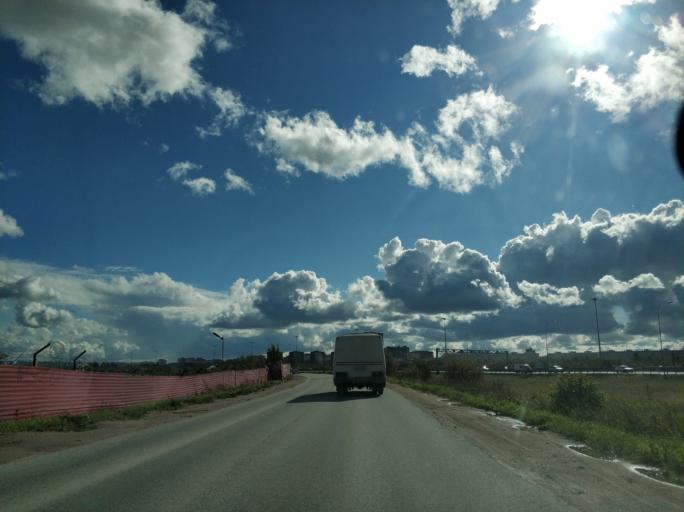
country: RU
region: Leningrad
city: Bugry
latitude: 60.0561
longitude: 30.3978
